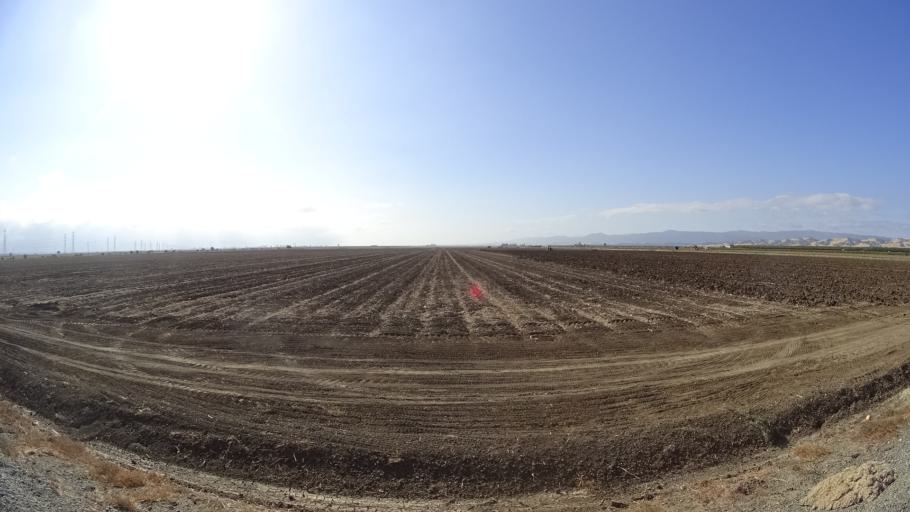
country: US
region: California
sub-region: Yolo County
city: Esparto
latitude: 38.7811
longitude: -122.0194
